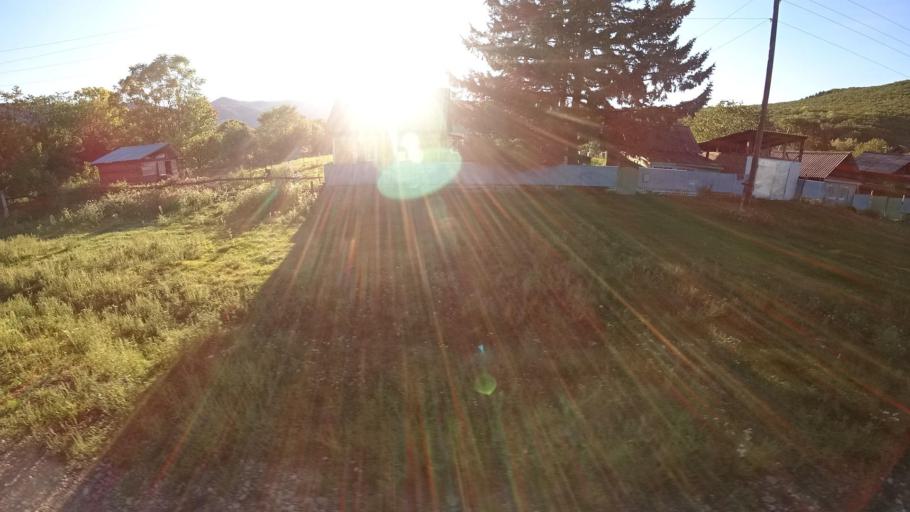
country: RU
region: Primorskiy
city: Kirovskiy
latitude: 44.8306
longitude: 133.5726
